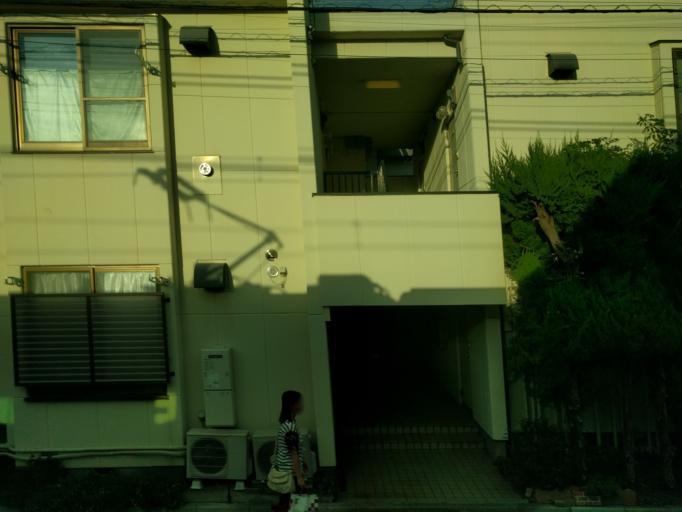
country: JP
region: Kanagawa
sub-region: Kawasaki-shi
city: Kawasaki
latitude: 35.5844
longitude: 139.6830
